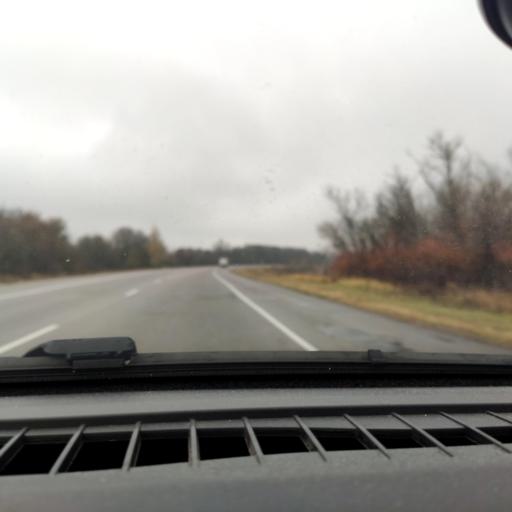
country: RU
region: Voronezj
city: Kolodeznyy
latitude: 51.3134
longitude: 39.0303
